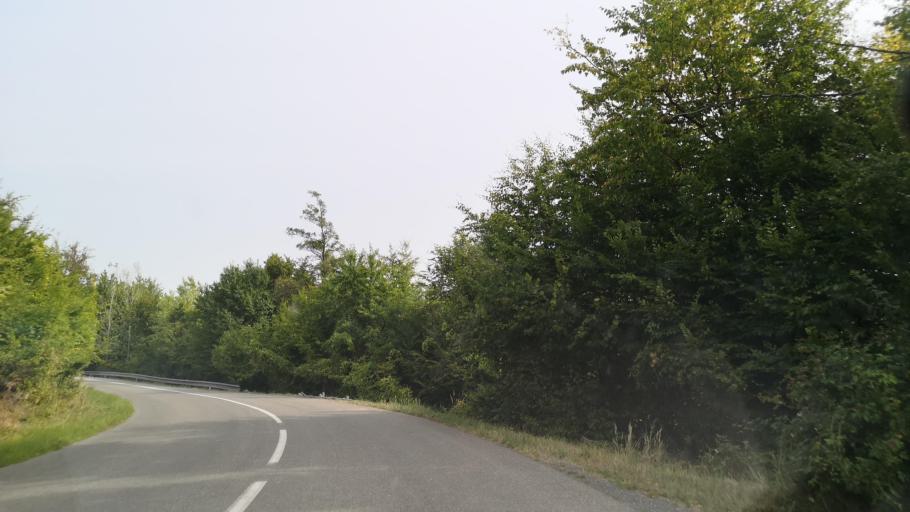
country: SK
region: Banskobystricky
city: Tisovec
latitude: 48.5650
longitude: 20.0305
